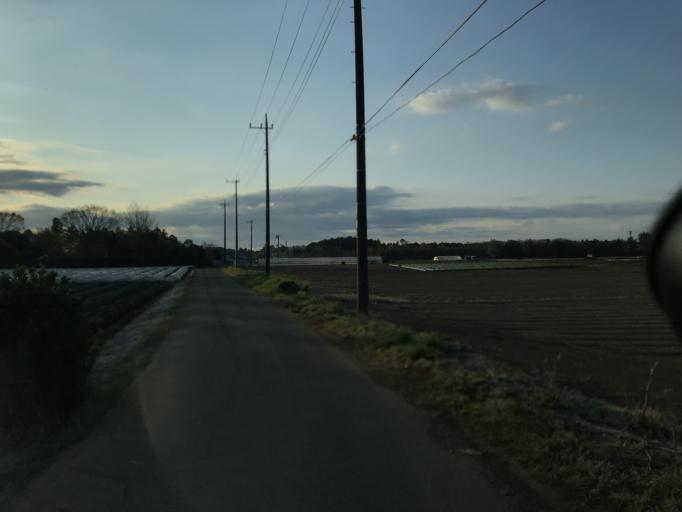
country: JP
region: Chiba
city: Omigawa
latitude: 35.7981
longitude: 140.5419
